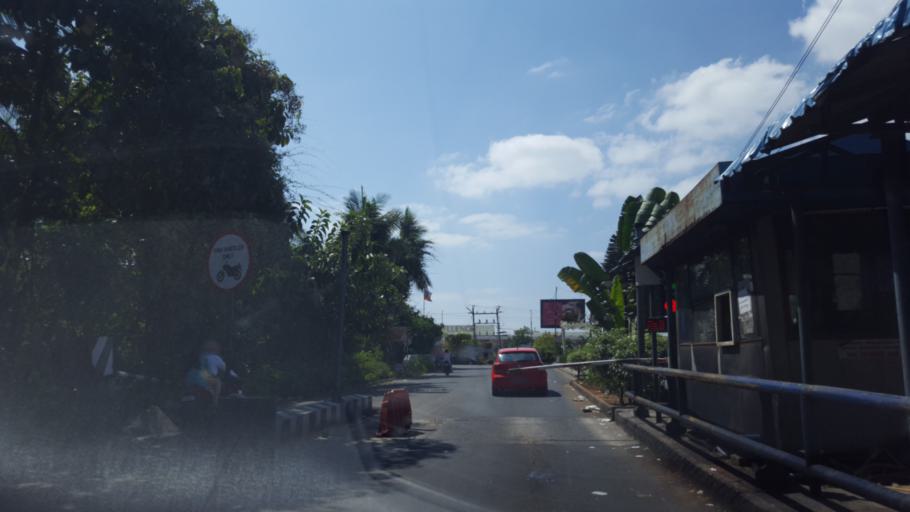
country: IN
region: Tamil Nadu
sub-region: Kancheepuram
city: Mamallapuram
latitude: 12.6155
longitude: 80.1699
